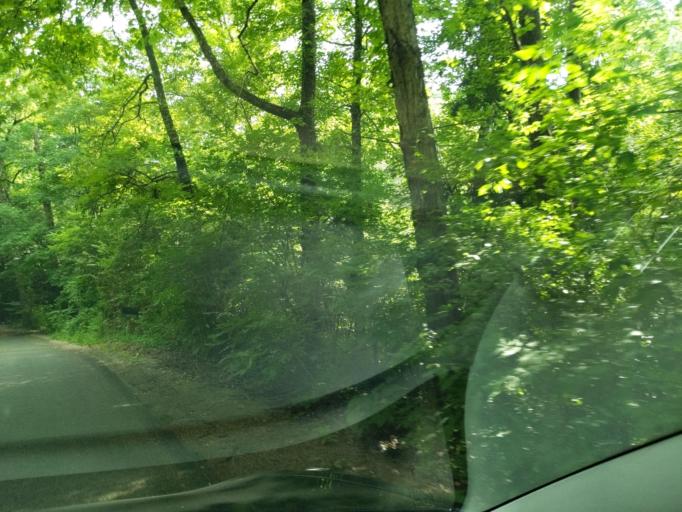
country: US
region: Ohio
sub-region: Fairfield County
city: Lancaster
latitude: 39.5857
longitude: -82.5542
